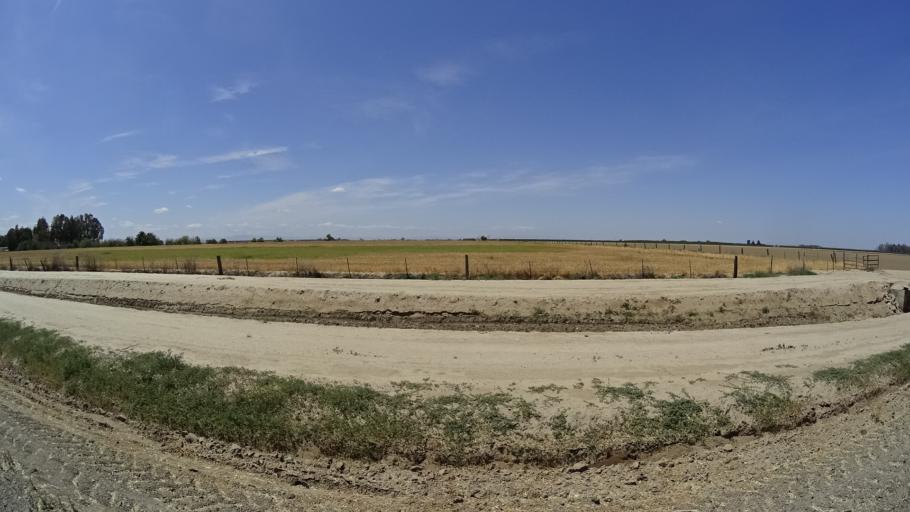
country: US
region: California
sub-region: Kings County
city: Home Garden
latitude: 36.2401
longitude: -119.6728
